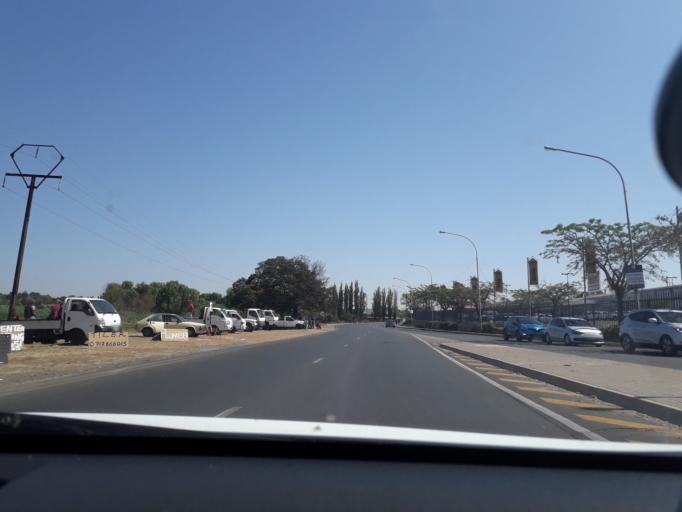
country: ZA
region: Gauteng
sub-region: City of Johannesburg Metropolitan Municipality
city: Modderfontein
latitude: -26.0980
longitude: 28.2204
